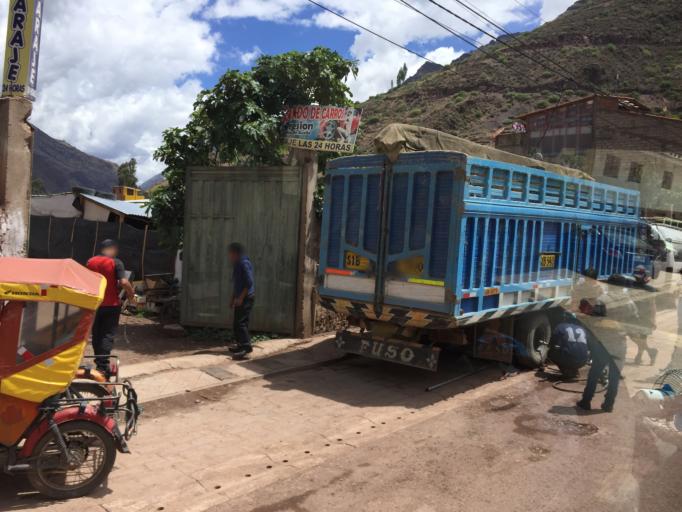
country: PE
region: Cusco
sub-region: Provincia de Calca
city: Pisac
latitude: -13.4227
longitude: -71.8490
